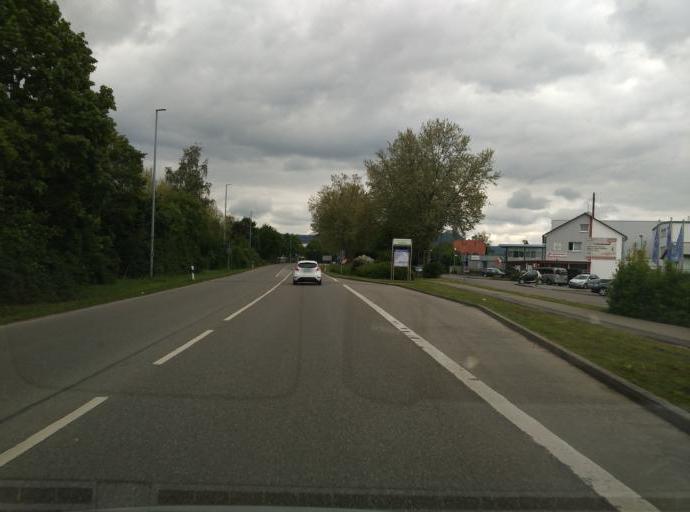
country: DE
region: Baden-Wuerttemberg
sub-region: Regierungsbezirk Stuttgart
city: Frickenhausen
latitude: 48.5998
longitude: 9.3516
